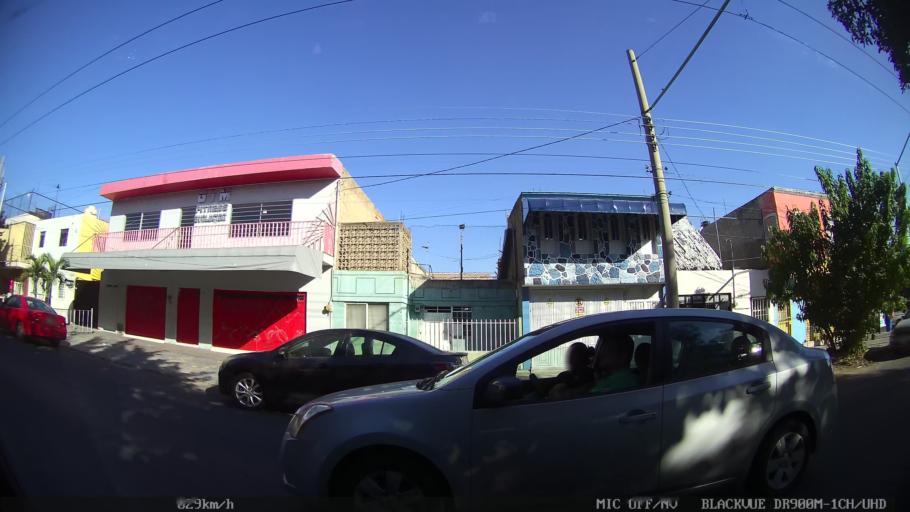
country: MX
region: Jalisco
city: Tlaquepaque
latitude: 20.6959
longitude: -103.3005
